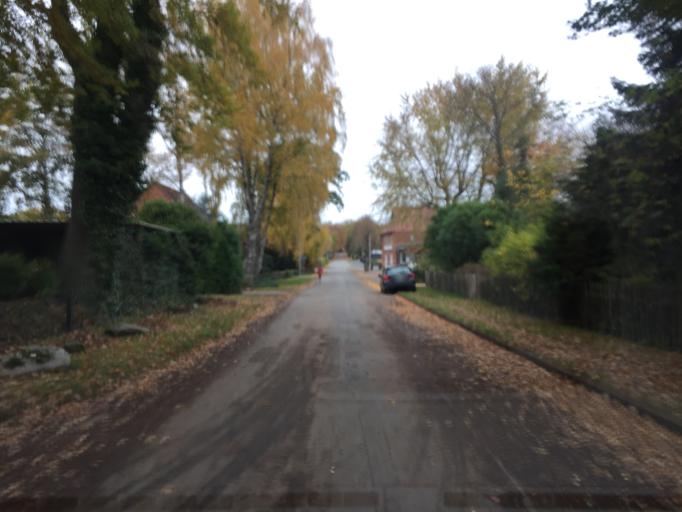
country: DE
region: Lower Saxony
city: Linsburg
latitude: 52.5917
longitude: 9.3067
